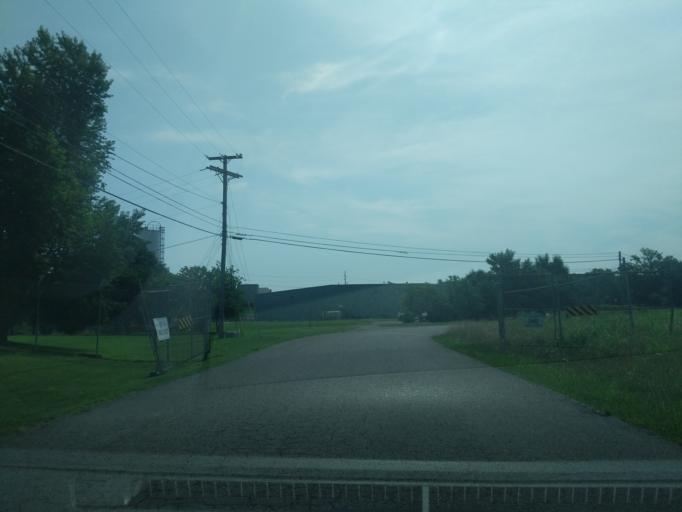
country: US
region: Tennessee
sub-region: Davidson County
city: Lakewood
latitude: 36.2673
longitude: -86.6605
